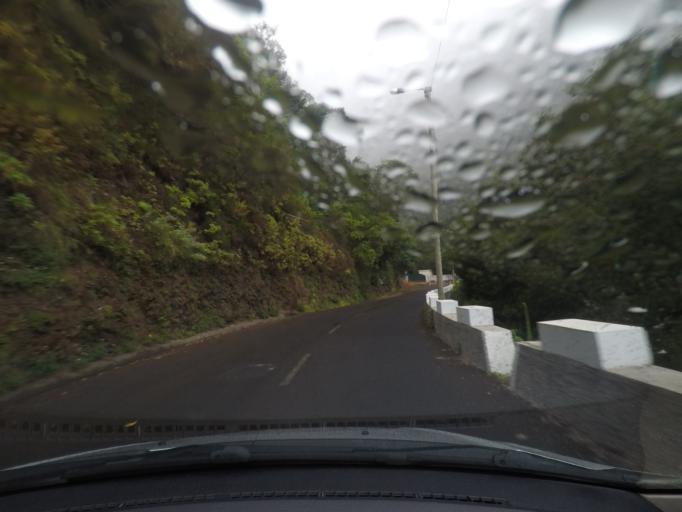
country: PT
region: Madeira
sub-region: Santana
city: Santana
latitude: 32.7539
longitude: -16.8799
